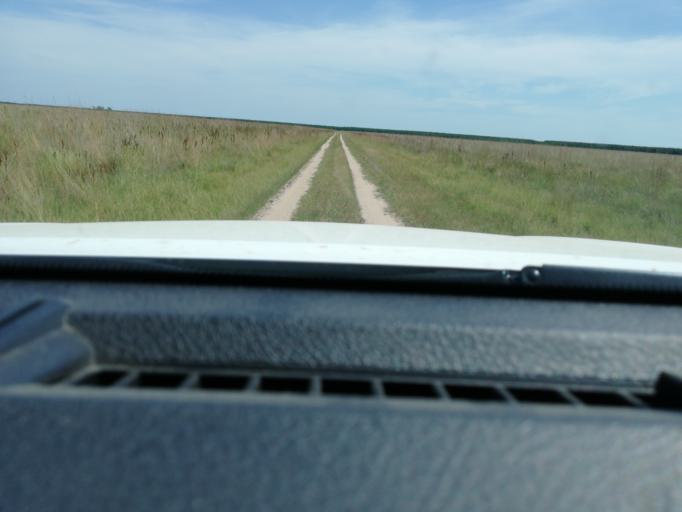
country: AR
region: Corrientes
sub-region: Departamento de San Miguel
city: San Miguel
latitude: -28.0540
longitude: -57.4552
